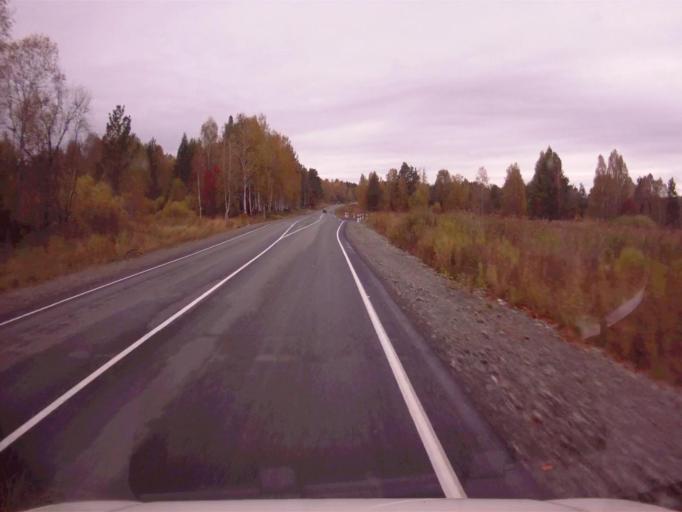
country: RU
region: Chelyabinsk
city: Nyazepetrovsk
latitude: 56.0445
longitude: 59.7664
